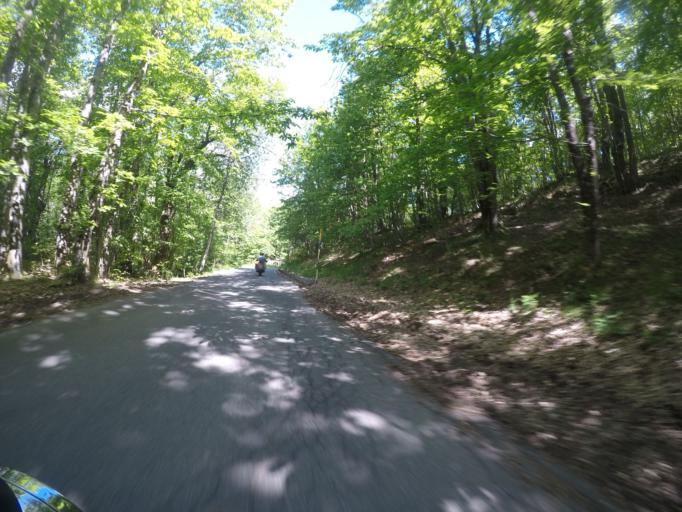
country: IT
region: Tuscany
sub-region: Provincia di Lucca
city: Careggine
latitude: 44.1123
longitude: 10.3315
